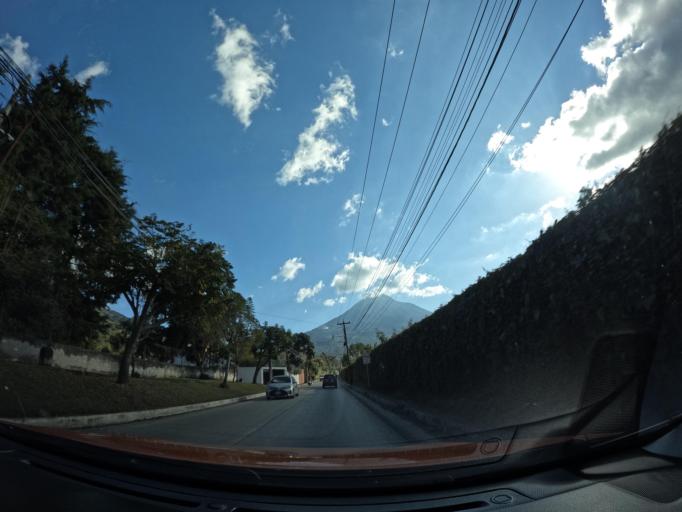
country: GT
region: Sacatepequez
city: Antigua Guatemala
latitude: 14.5416
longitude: -90.7294
